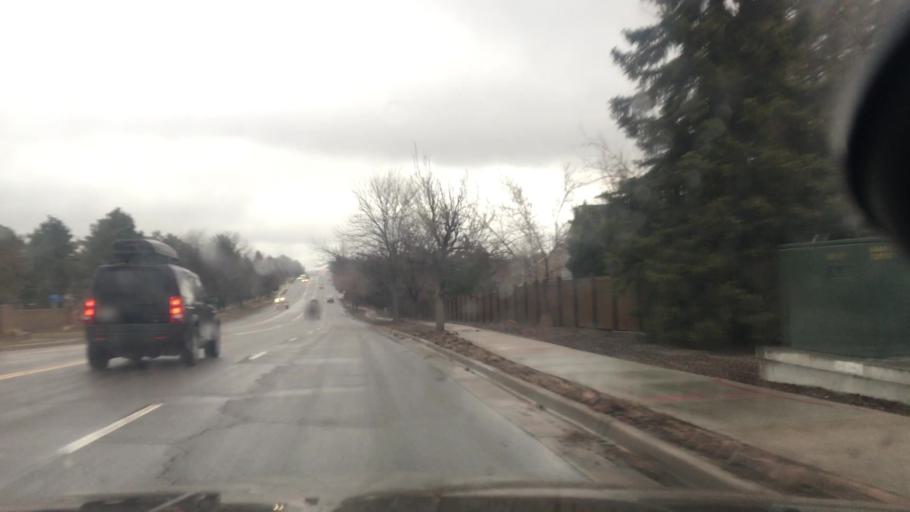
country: US
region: Colorado
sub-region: Arapahoe County
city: Castlewood
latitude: 39.5737
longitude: -104.9229
